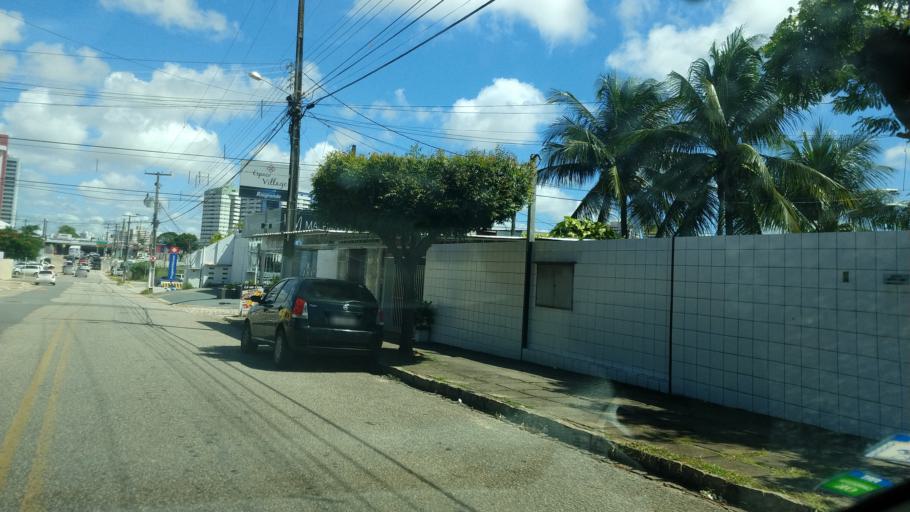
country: BR
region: Rio Grande do Norte
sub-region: Natal
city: Natal
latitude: -5.8509
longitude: -35.2015
